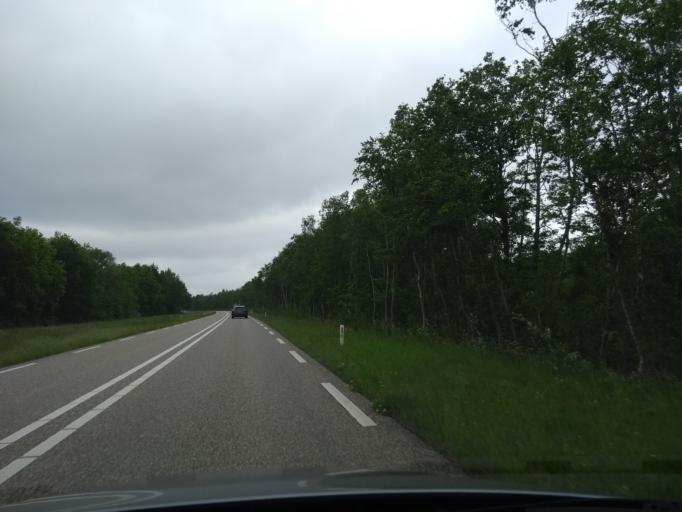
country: NL
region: Friesland
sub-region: Gemeente Dongeradeel
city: Anjum
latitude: 53.4013
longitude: 6.2315
